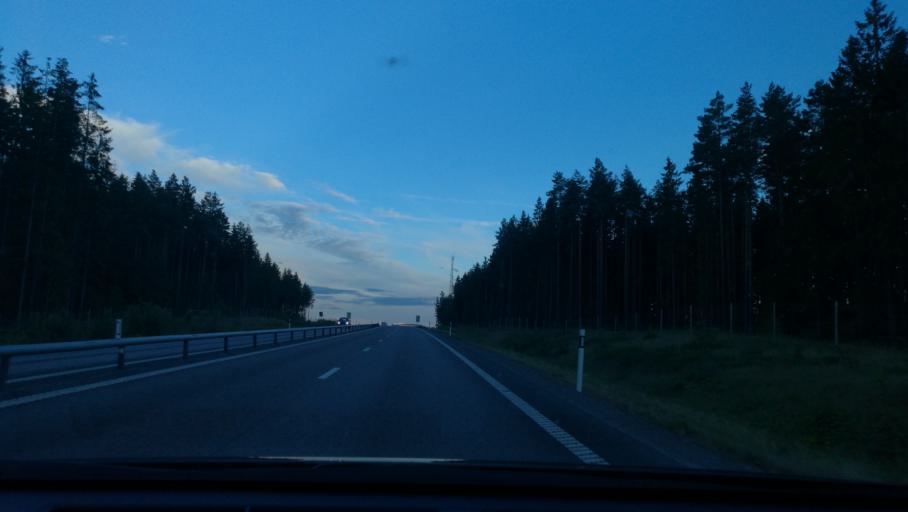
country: SE
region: Soedermanland
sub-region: Katrineholms Kommun
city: Katrineholm
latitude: 59.0040
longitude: 16.2455
